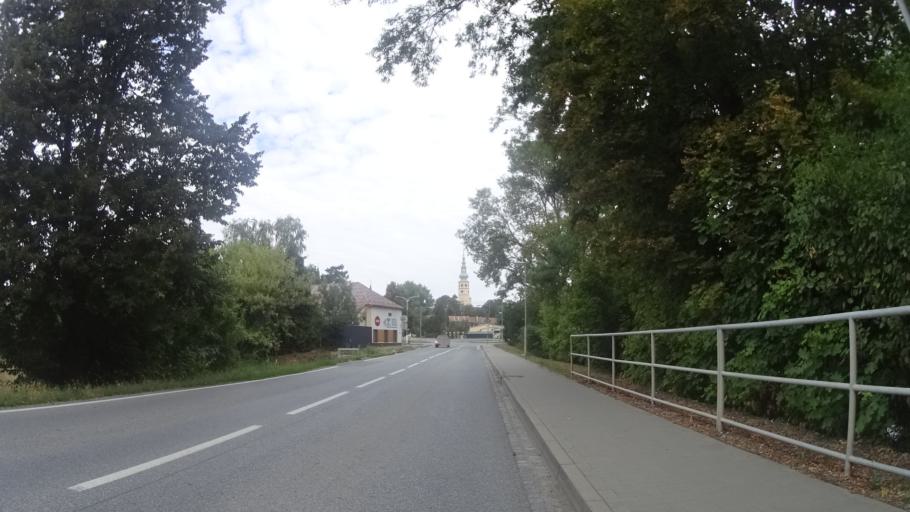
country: CZ
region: Olomoucky
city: Tovacov
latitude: 49.4254
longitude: 17.2913
